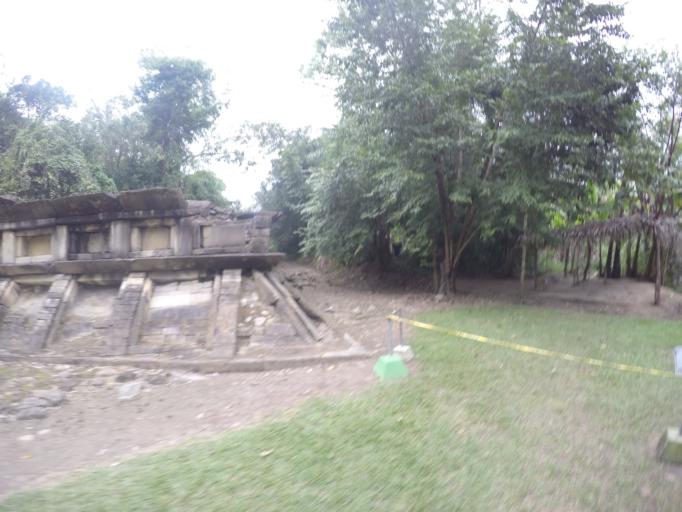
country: MX
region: Veracruz
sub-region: Papantla
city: El Chote
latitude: 20.4417
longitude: -97.3785
